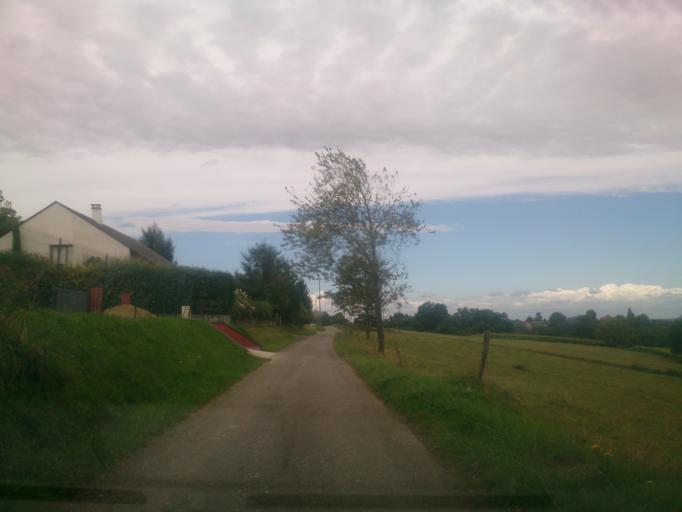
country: FR
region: Midi-Pyrenees
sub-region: Departement des Hautes-Pyrenees
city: Horgues
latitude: 43.1377
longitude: 0.0758
